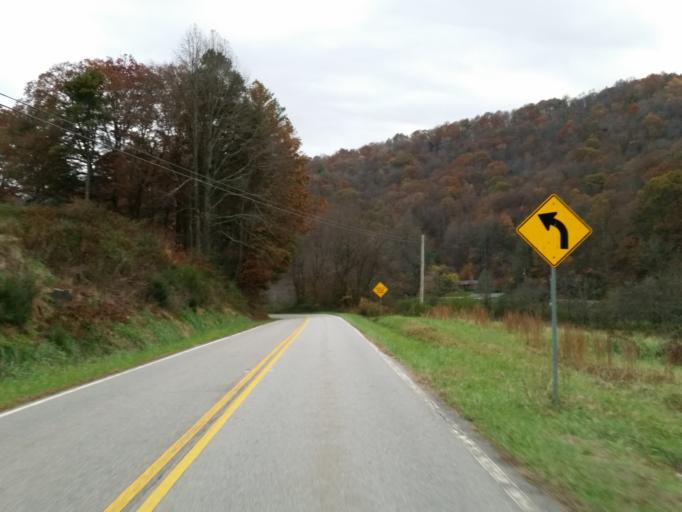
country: US
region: Georgia
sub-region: Union County
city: Blairsville
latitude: 34.7247
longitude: -84.0809
